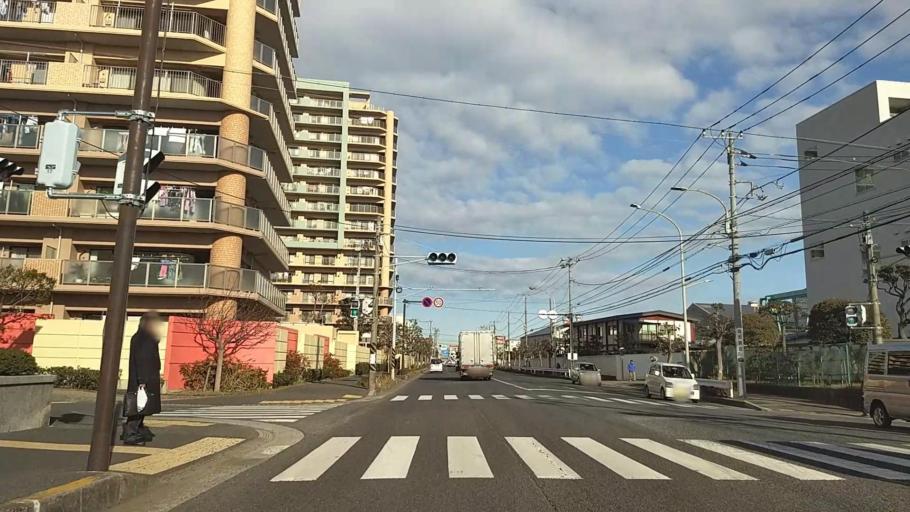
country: JP
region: Kanagawa
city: Hiratsuka
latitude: 35.3258
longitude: 139.3603
